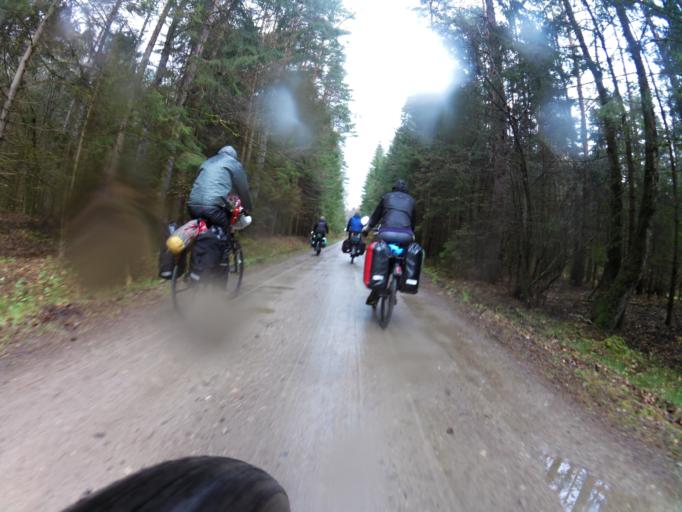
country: PL
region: Pomeranian Voivodeship
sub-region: Powiat slupski
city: Kepice
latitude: 54.2647
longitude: 16.7963
